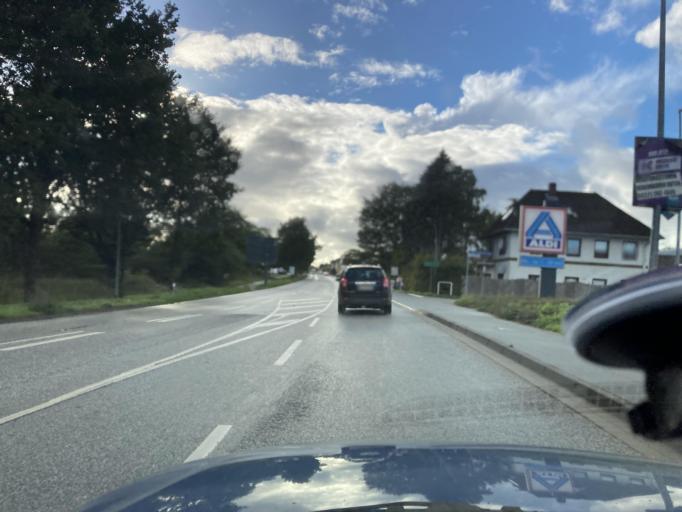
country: DE
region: Schleswig-Holstein
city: Heide
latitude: 54.1977
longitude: 9.1212
